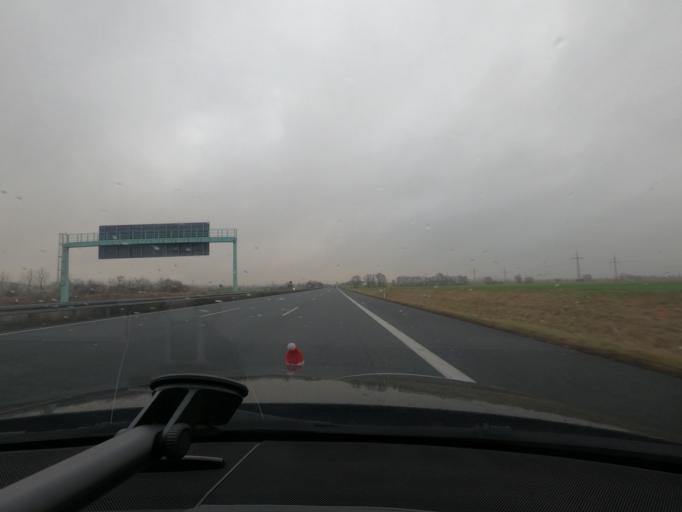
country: DE
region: Lower Saxony
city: Rosdorf
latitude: 51.4702
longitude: 9.8719
